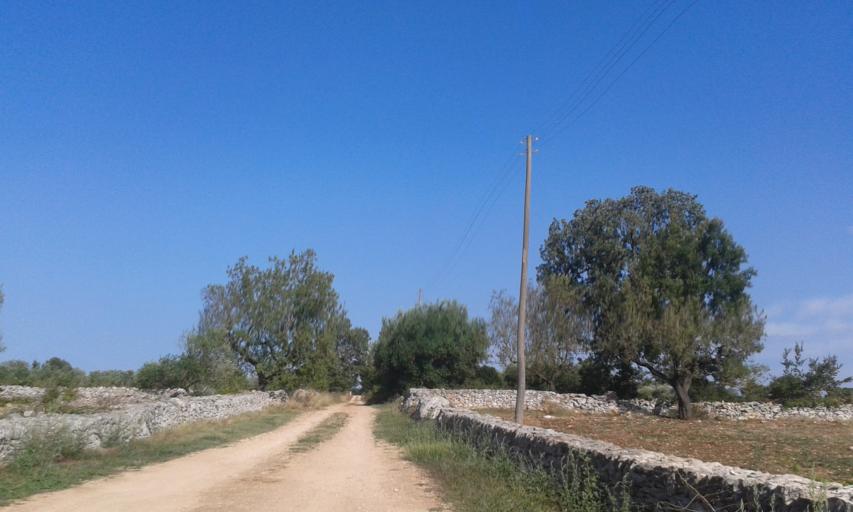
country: IT
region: Apulia
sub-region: Provincia di Bari
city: Gioia del Colle
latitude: 40.7750
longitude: 16.9676
